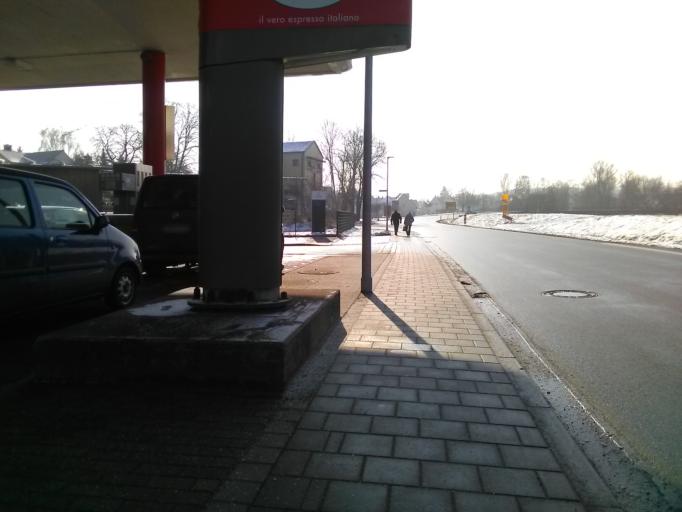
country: DE
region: Bavaria
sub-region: Regierungsbezirk Mittelfranken
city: Windsbach
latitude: 49.2489
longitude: 10.8238
